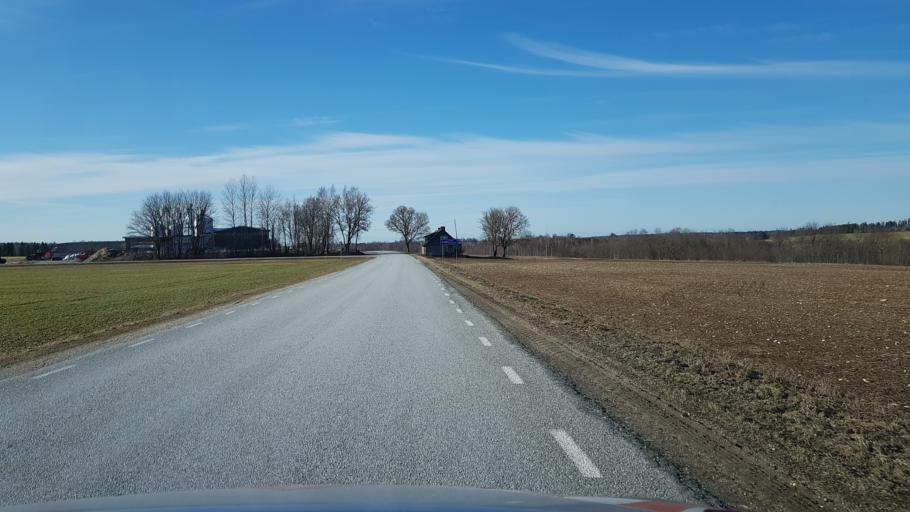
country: EE
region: Laeaene-Virumaa
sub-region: Kadrina vald
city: Kadrina
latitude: 59.2909
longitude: 26.1753
